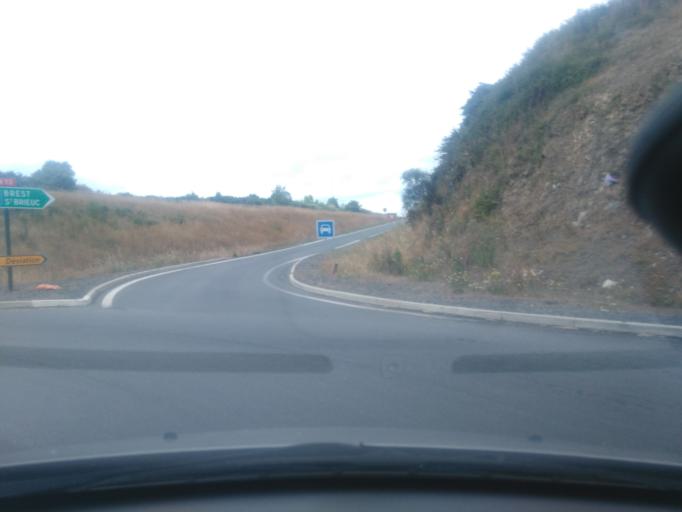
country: FR
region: Brittany
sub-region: Departement des Cotes-d'Armor
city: Yffiniac
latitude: 48.4831
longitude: -2.6894
